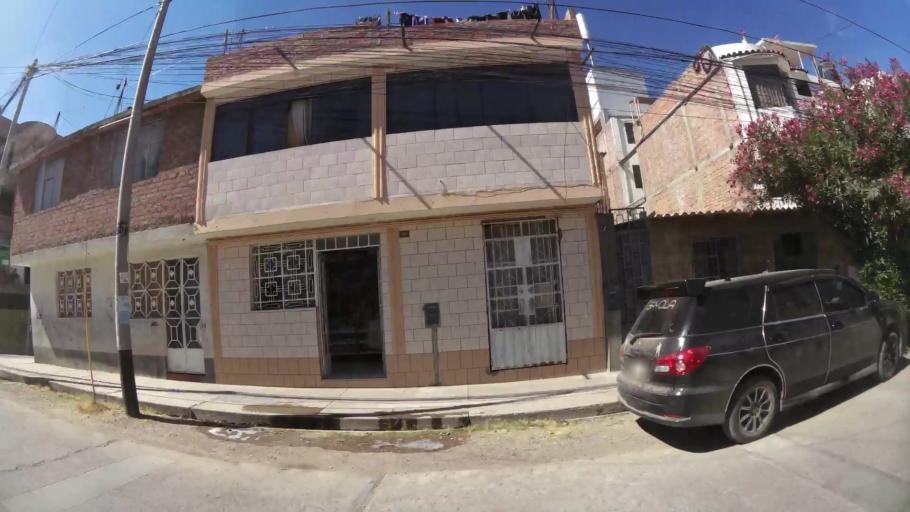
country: PE
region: Ayacucho
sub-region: Provincia de Huamanga
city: Ayacucho
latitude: -13.1486
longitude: -74.2264
